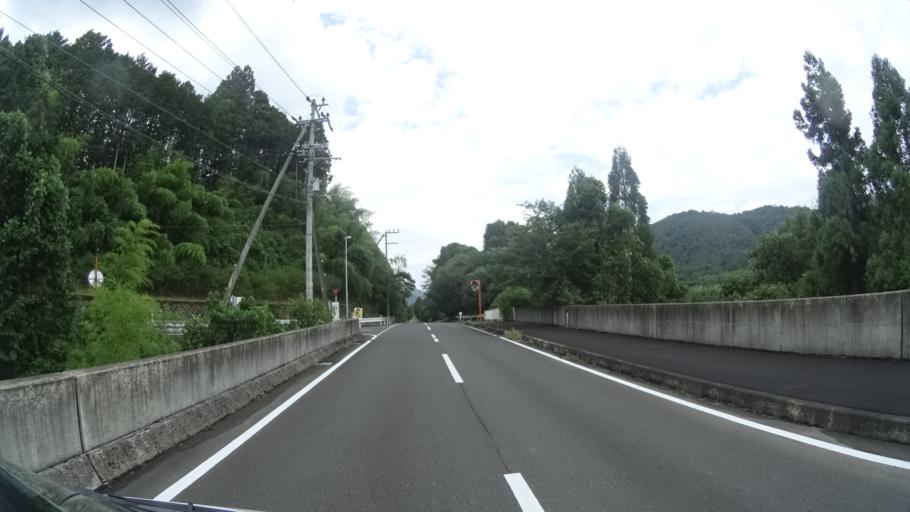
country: JP
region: Kyoto
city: Ayabe
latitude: 35.2860
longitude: 135.2881
